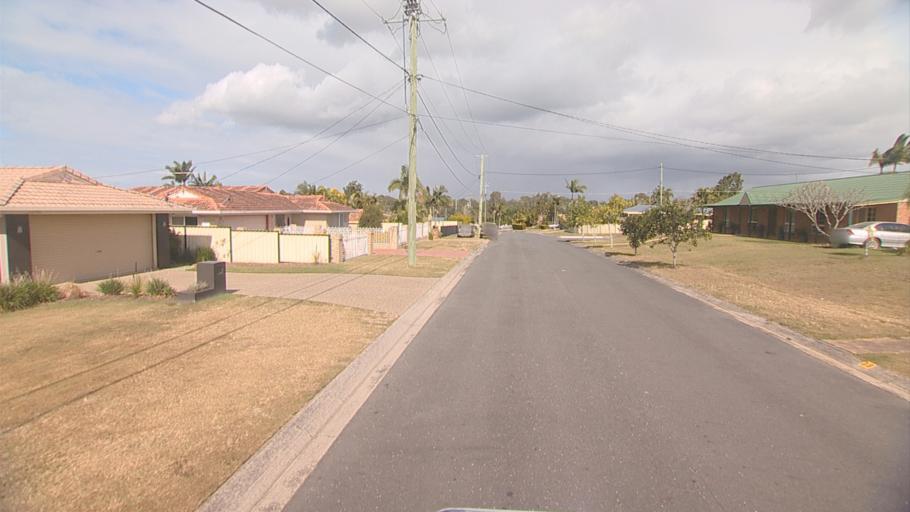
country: AU
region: Queensland
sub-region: Logan
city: Park Ridge South
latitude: -27.6773
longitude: 153.0340
